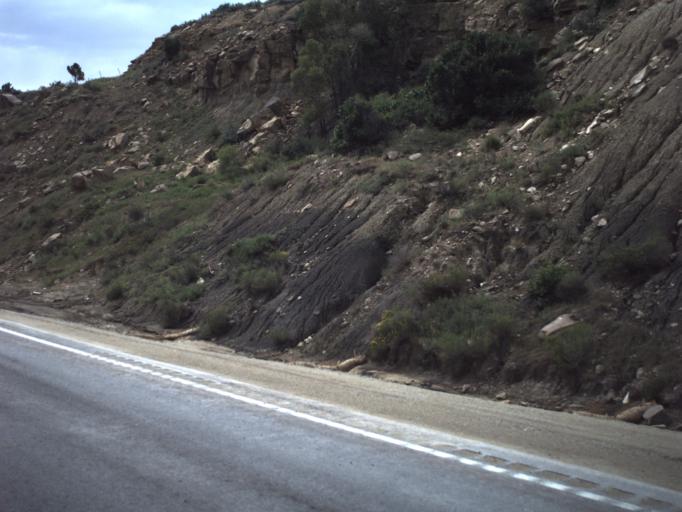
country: US
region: Utah
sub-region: Carbon County
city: Helper
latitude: 39.7844
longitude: -110.9252
